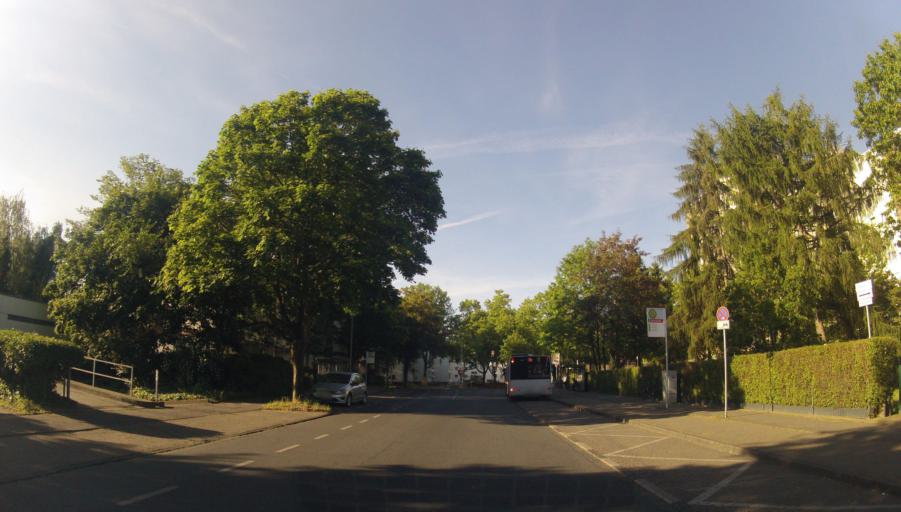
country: DE
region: North Rhine-Westphalia
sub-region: Regierungsbezirk Dusseldorf
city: Ratingen
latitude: 51.2958
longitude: 6.8178
